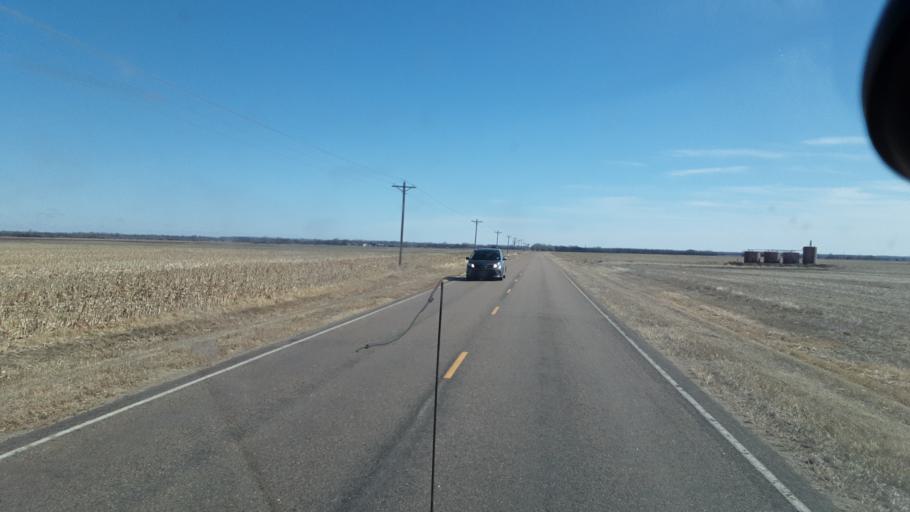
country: US
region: Kansas
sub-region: Reno County
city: Nickerson
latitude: 38.2177
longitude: -98.0992
